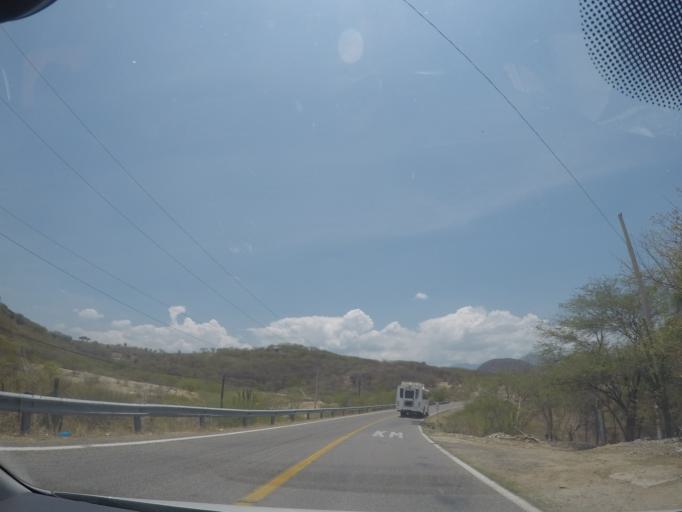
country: MX
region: Oaxaca
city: Magdalena Tequisistlan
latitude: 16.4097
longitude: -95.5929
